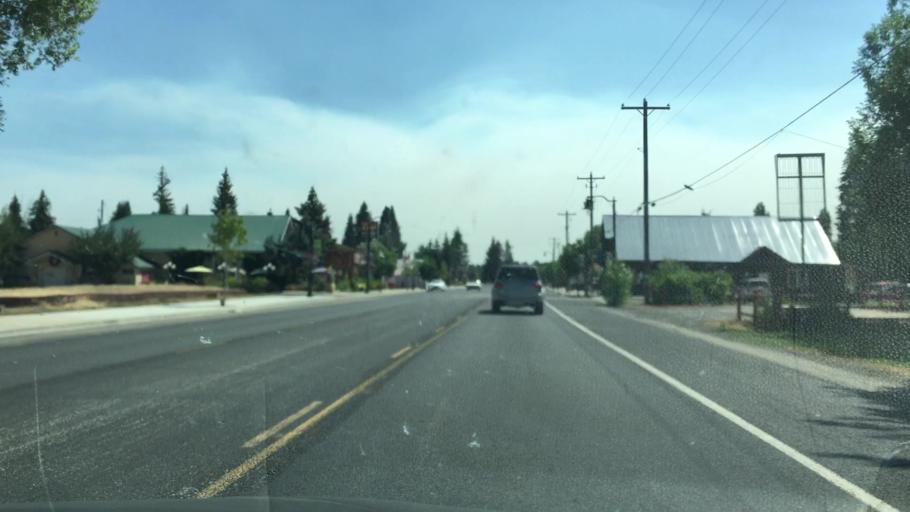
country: US
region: Idaho
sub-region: Valley County
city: McCall
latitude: 44.7336
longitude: -116.0784
